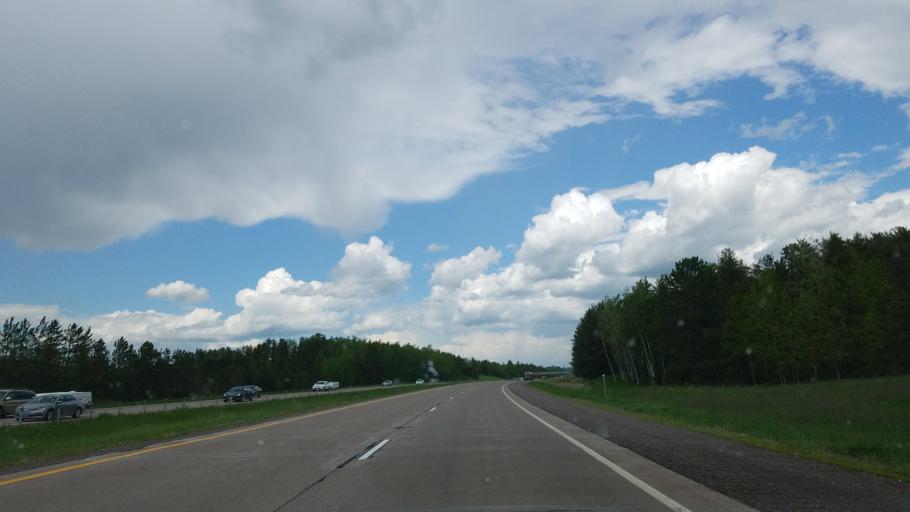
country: US
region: Minnesota
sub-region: Carlton County
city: Moose Lake
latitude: 46.4849
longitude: -92.7070
